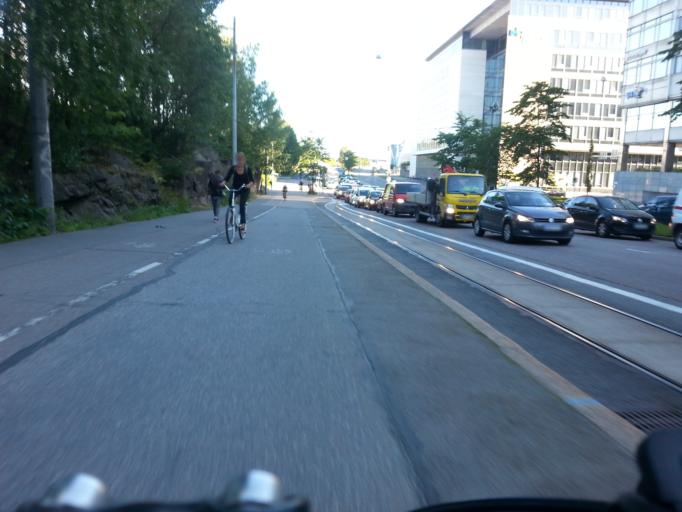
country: FI
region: Uusimaa
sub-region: Helsinki
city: Helsinki
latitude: 60.2004
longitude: 24.9340
